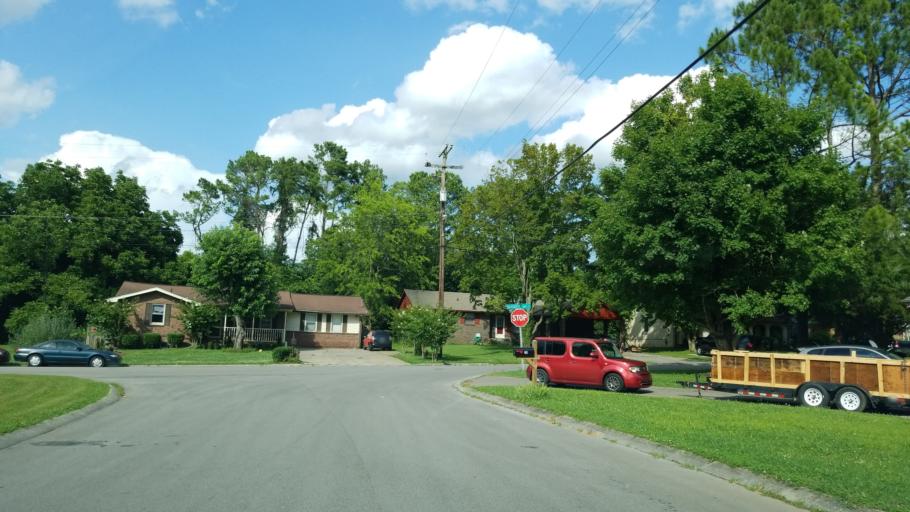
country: US
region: Tennessee
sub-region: Rutherford County
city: La Vergne
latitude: 36.0540
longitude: -86.6755
